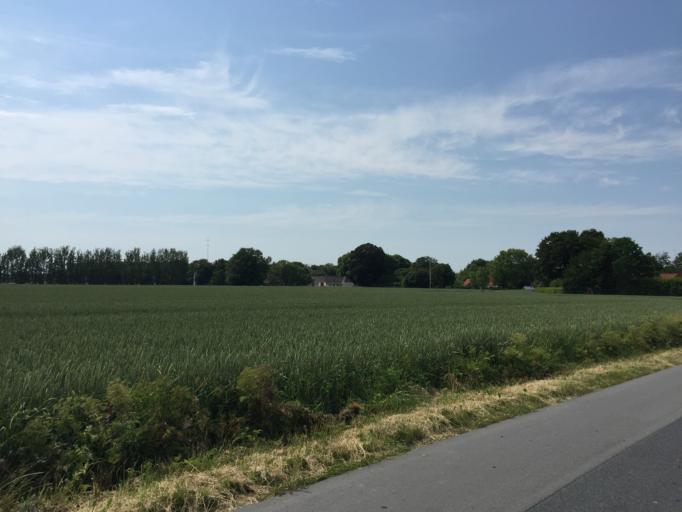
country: DK
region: South Denmark
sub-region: Nyborg Kommune
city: Ullerslev
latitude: 55.3966
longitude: 10.6767
